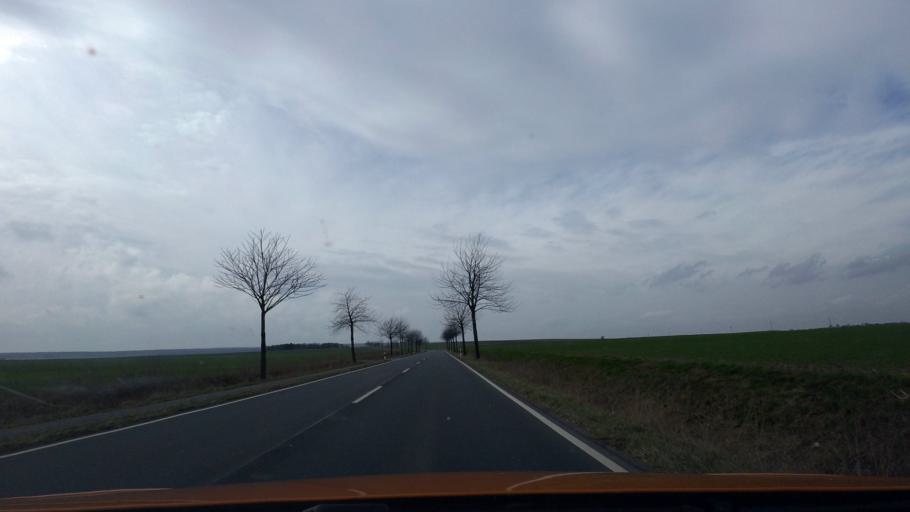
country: DE
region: Lower Saxony
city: Supplingen
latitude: 52.2275
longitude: 10.8919
